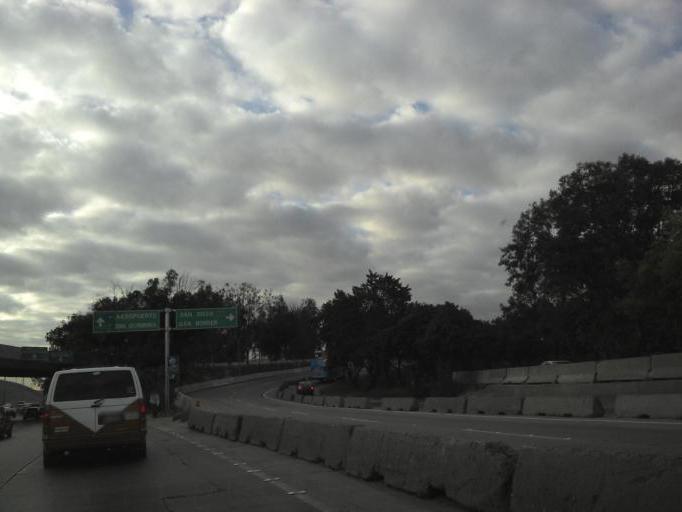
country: MX
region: Baja California
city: Tijuana
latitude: 32.5349
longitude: -117.0285
